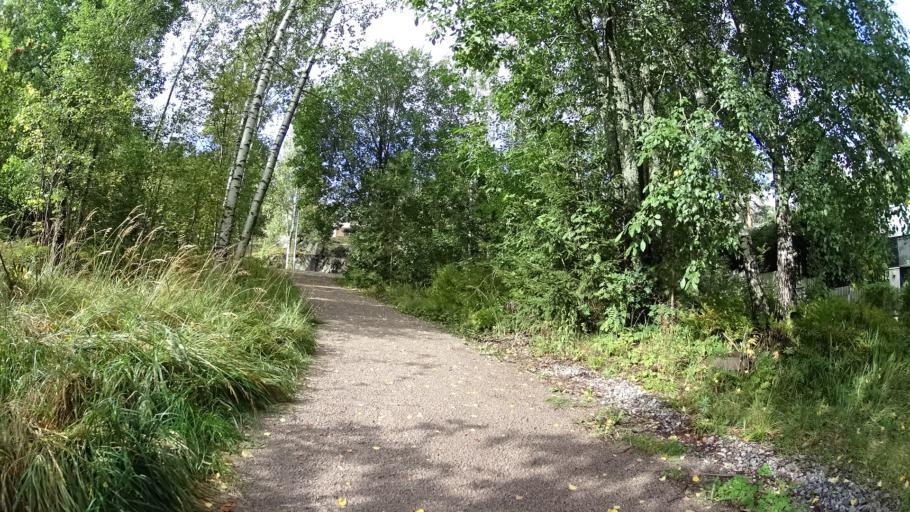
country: FI
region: Uusimaa
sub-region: Helsinki
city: Kilo
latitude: 60.1927
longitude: 24.7600
